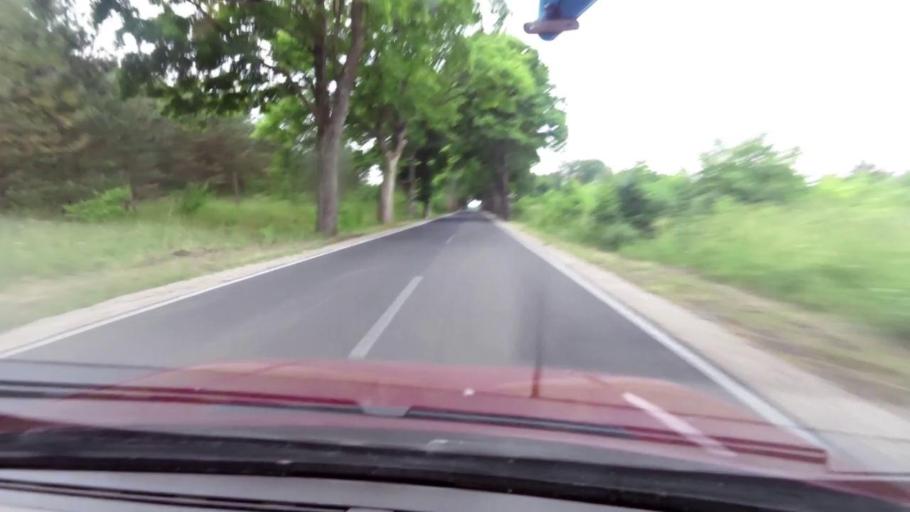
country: PL
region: West Pomeranian Voivodeship
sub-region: Powiat koszalinski
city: Sianow
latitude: 54.1558
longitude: 16.4598
